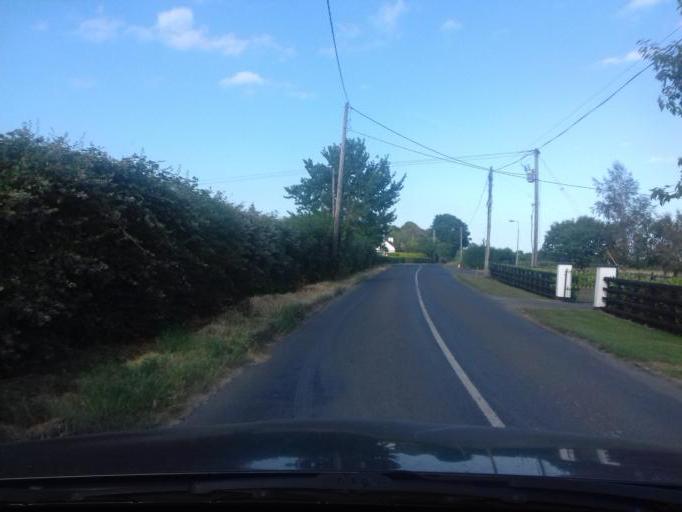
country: IE
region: Leinster
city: Hartstown
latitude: 53.4477
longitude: -6.4147
